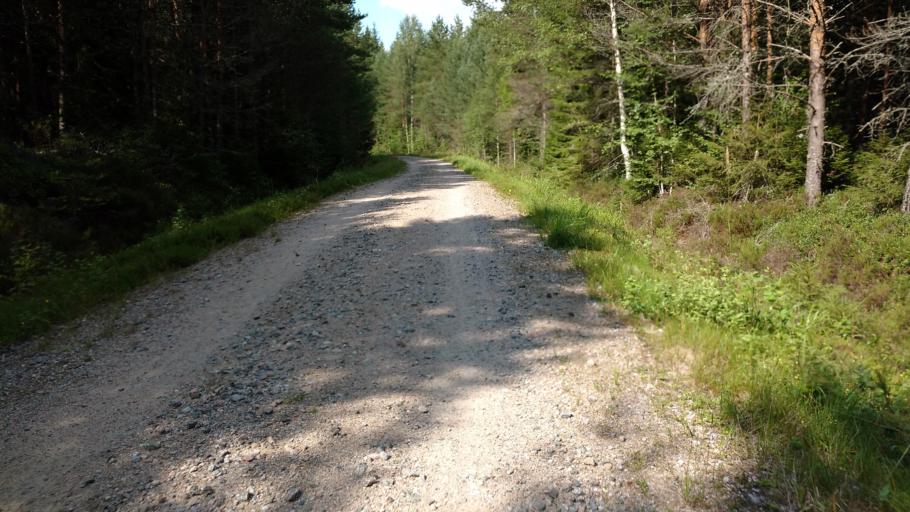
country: FI
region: Varsinais-Suomi
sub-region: Salo
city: Pertteli
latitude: 60.3992
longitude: 23.2191
